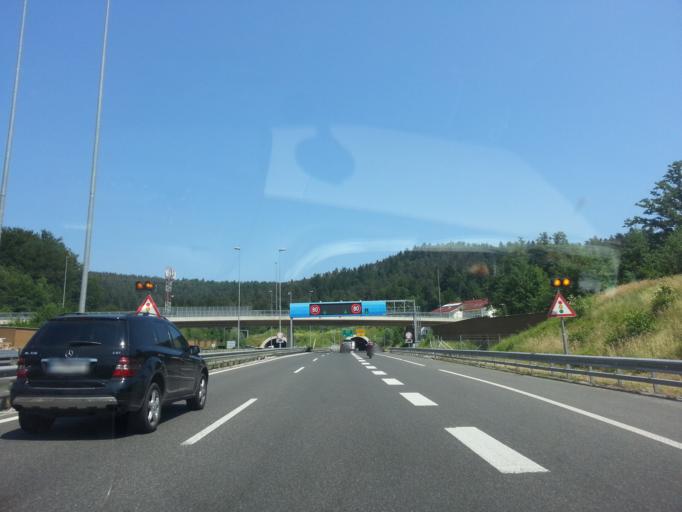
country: SI
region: Ljubljana
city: Ljubljana
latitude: 46.0855
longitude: 14.4605
